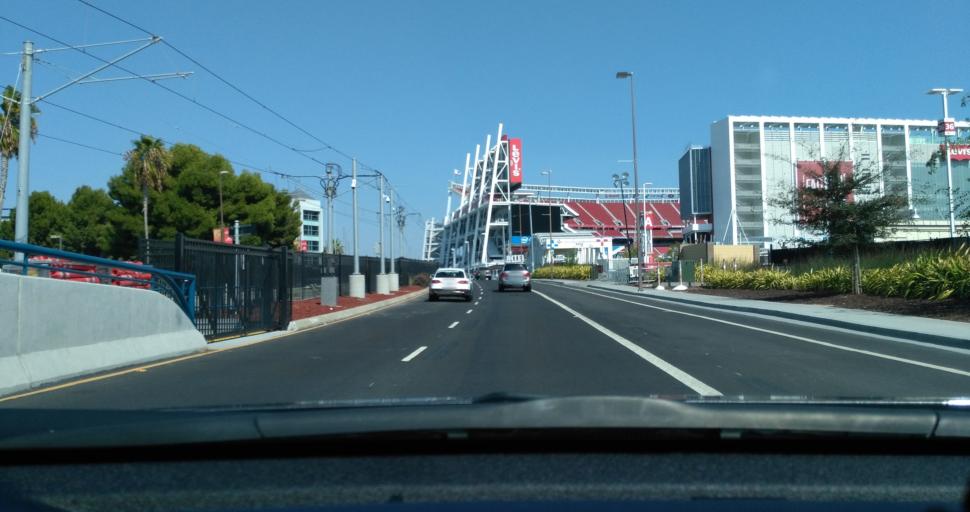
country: US
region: California
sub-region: Santa Clara County
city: Santa Clara
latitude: 37.4034
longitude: -121.9741
